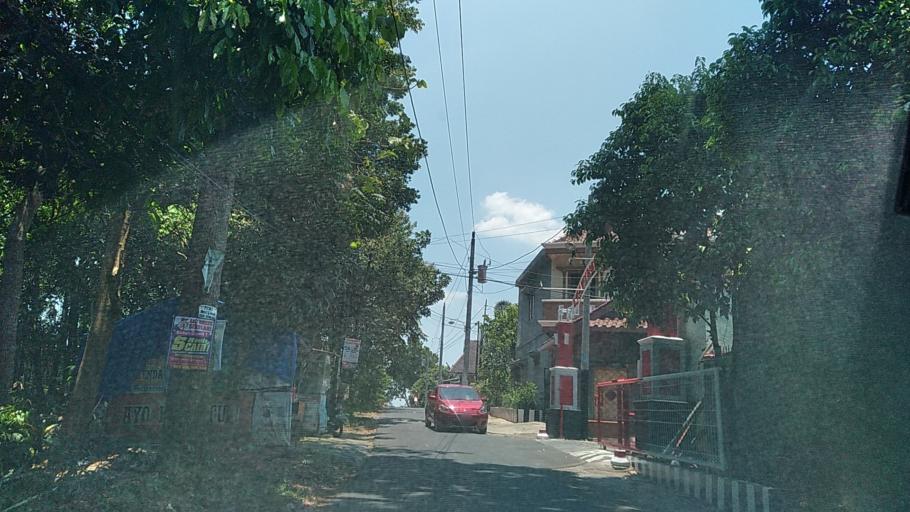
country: ID
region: Central Java
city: Ungaran
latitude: -7.0803
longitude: 110.4237
